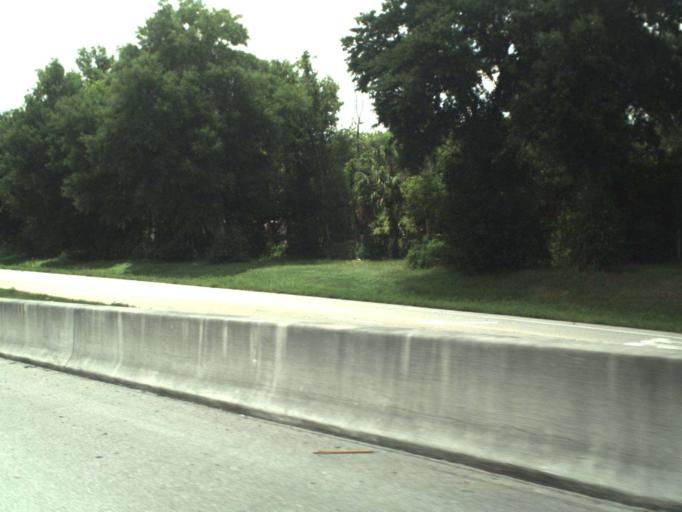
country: US
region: Florida
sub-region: Orange County
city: Lockhart
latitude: 28.6408
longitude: -81.4174
